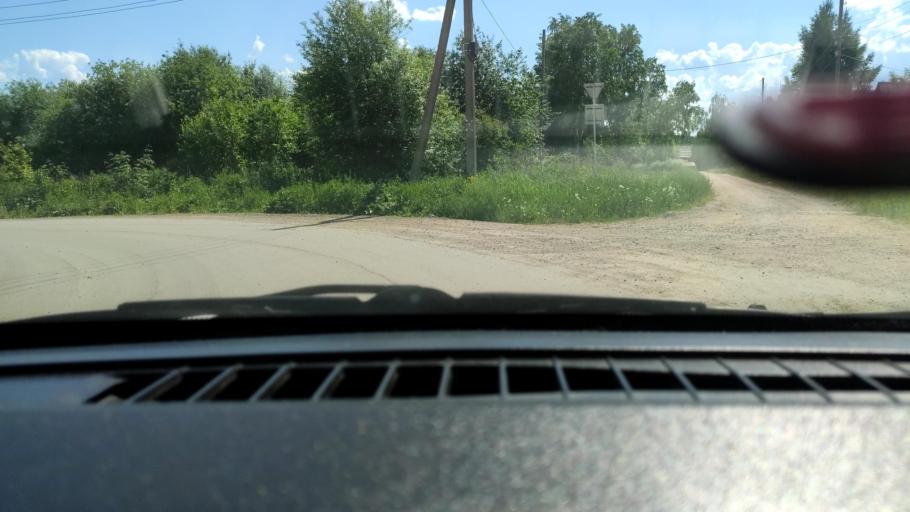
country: RU
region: Perm
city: Sylva
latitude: 58.0346
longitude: 56.7739
